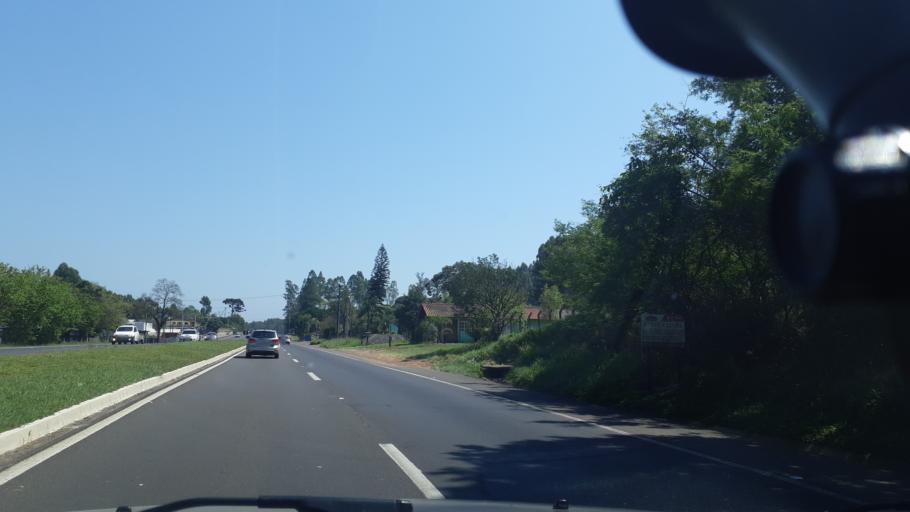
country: BR
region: Rio Grande do Sul
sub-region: Portao
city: Portao
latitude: -29.6382
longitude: -51.2944
